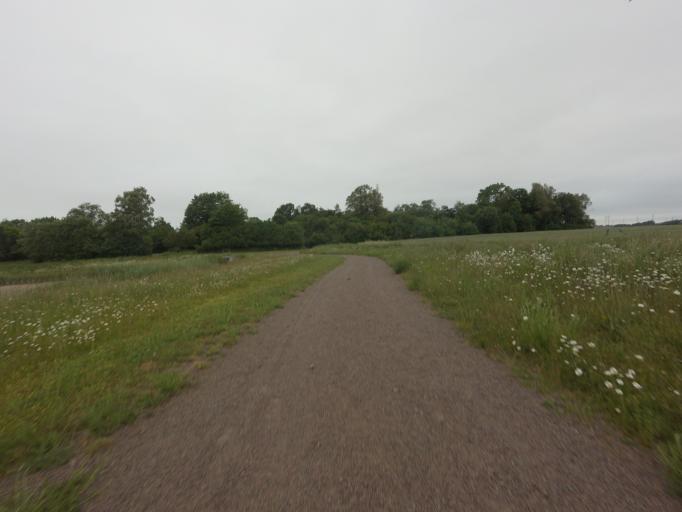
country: SE
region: Skane
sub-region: Angelholms Kommun
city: Strovelstorp
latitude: 56.1466
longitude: 12.7815
